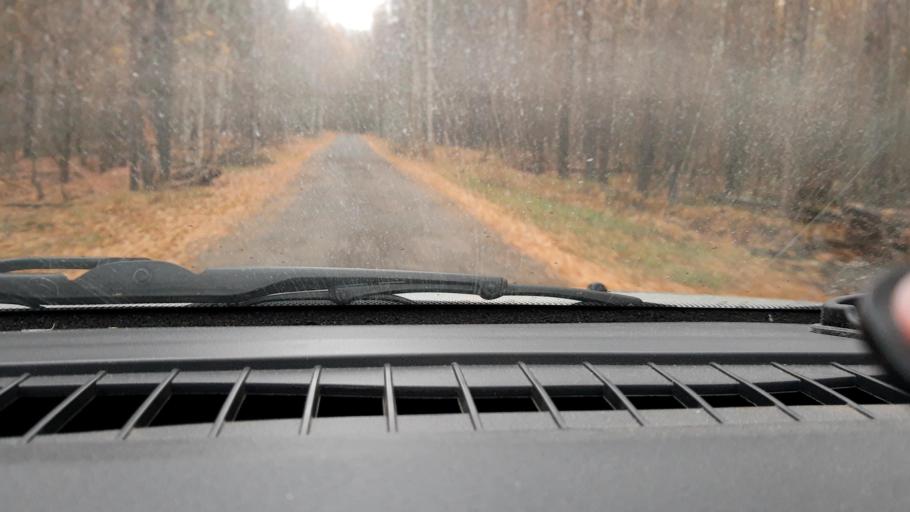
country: RU
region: Nizjnij Novgorod
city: Sitniki
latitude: 56.4202
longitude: 44.0464
